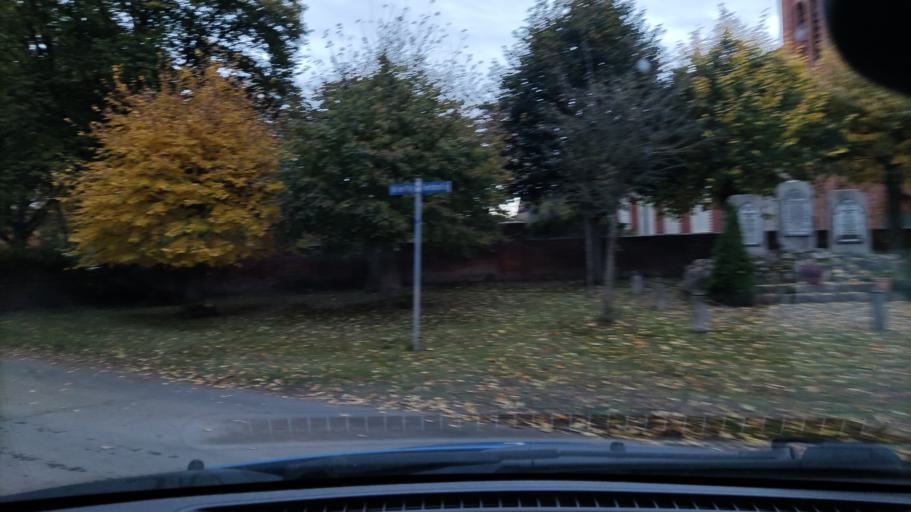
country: DE
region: Lower Saxony
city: Prezelle
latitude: 52.9626
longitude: 11.4022
